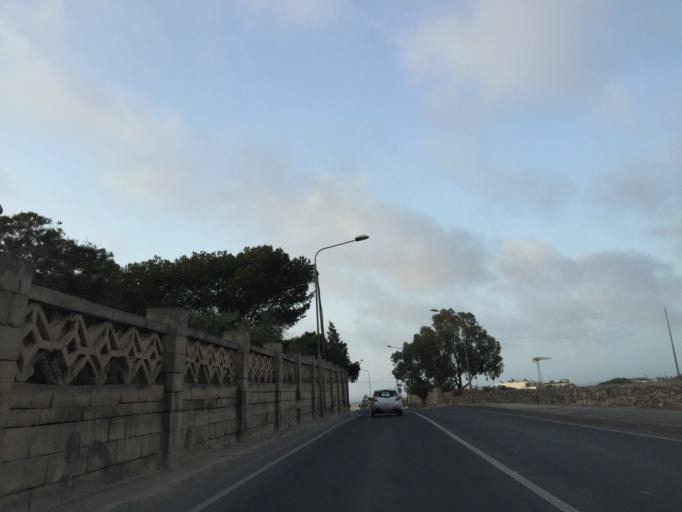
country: MT
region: Il-Mosta
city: Mosta
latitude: 35.9136
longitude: 14.4151
